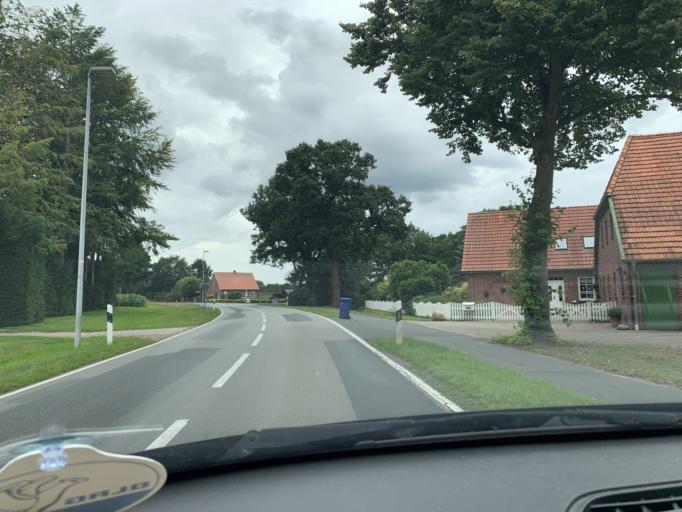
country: DE
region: Lower Saxony
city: Edewecht
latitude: 53.1297
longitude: 7.8949
